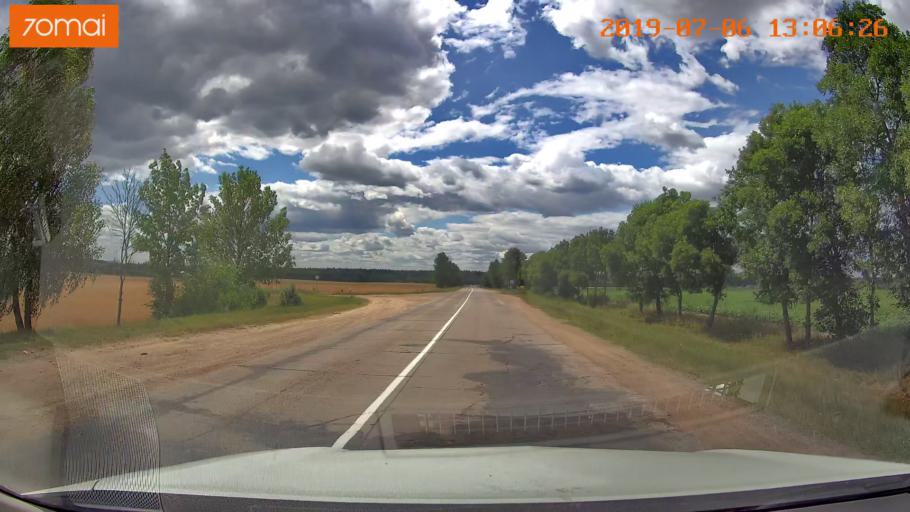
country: BY
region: Minsk
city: Dzyarzhynsk
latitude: 53.6811
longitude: 27.0535
